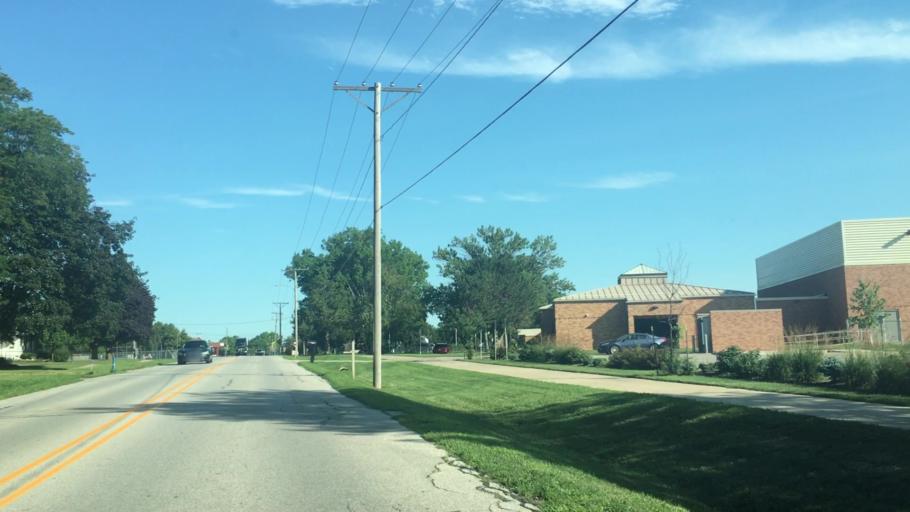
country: US
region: Iowa
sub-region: Johnson County
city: North Liberty
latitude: 41.7466
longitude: -91.5947
